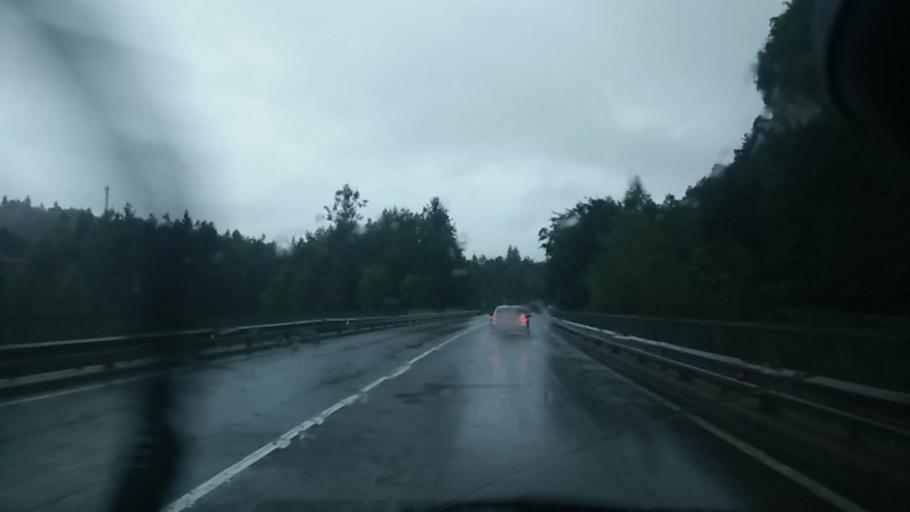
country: AT
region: Carinthia
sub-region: Politischer Bezirk Villach Land
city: Finkenstein am Faaker See
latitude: 46.5759
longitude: 13.8356
